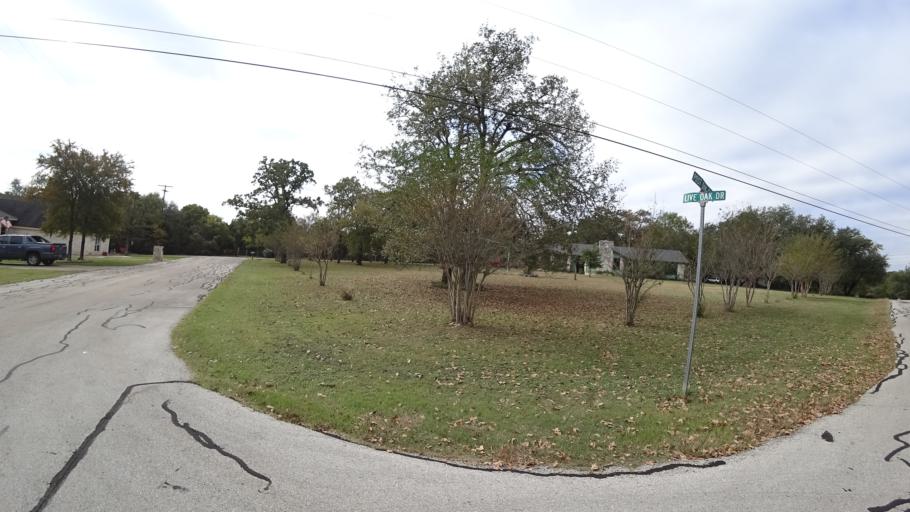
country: US
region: Texas
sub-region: Travis County
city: Shady Hollow
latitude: 30.1347
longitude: -97.8948
